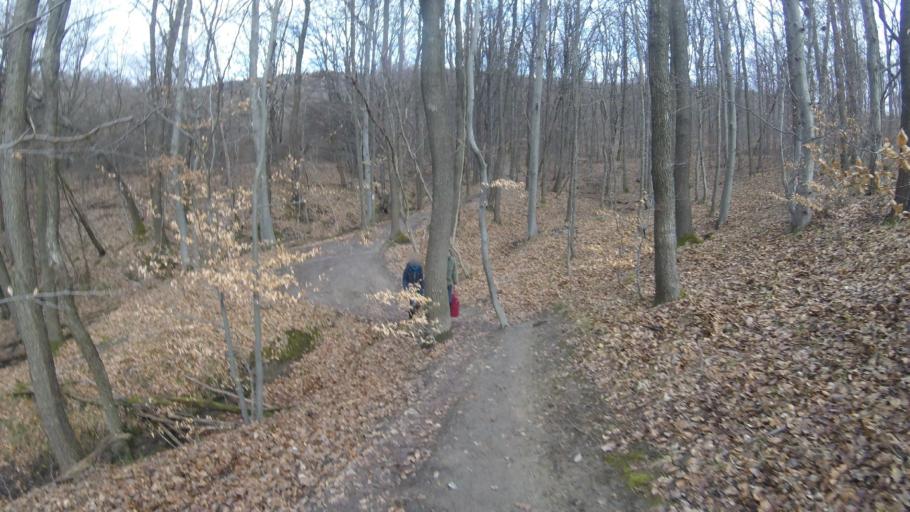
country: HU
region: Pest
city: Pilisszentkereszt
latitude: 47.6937
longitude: 18.9161
